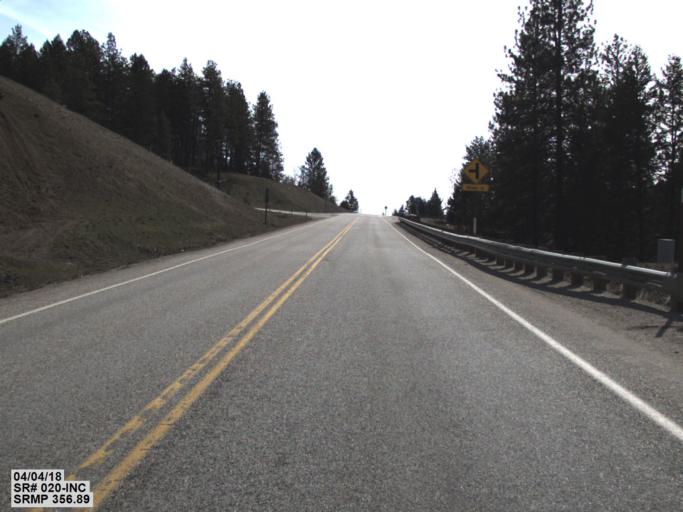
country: US
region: Washington
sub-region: Stevens County
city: Colville
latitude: 48.5442
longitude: -117.8528
